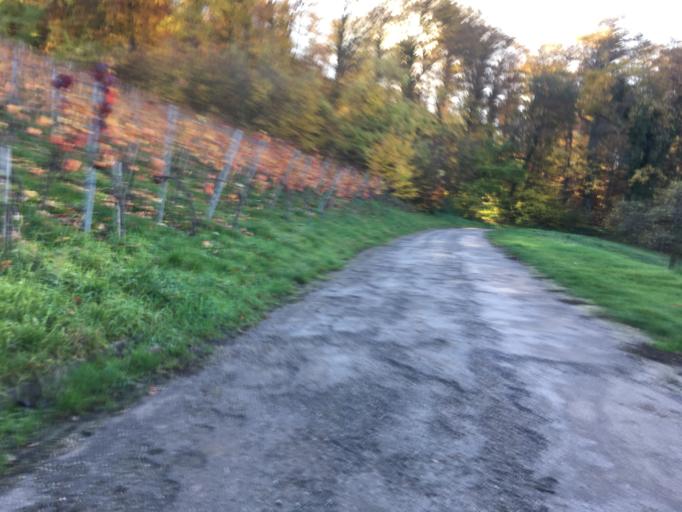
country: DE
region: Baden-Wuerttemberg
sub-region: Karlsruhe Region
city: Oberderdingen
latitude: 49.0486
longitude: 8.8035
